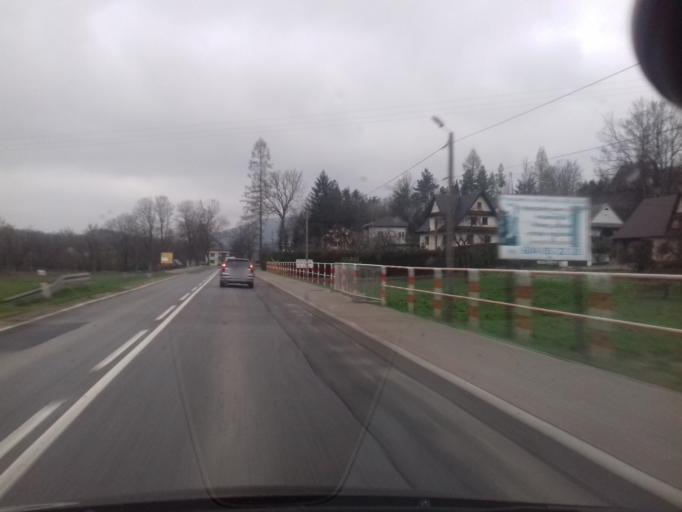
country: PL
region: Lesser Poland Voivodeship
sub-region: Powiat limanowski
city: Mszana Dolna
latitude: 49.6922
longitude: 20.0442
